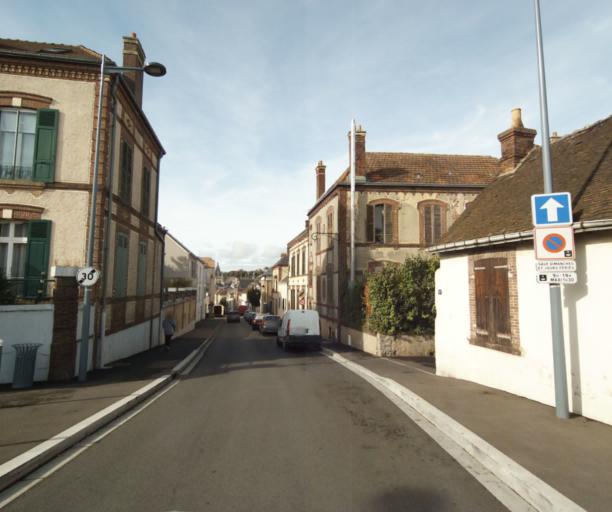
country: FR
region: Centre
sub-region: Departement d'Eure-et-Loir
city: Dreux
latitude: 48.7332
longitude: 1.3731
